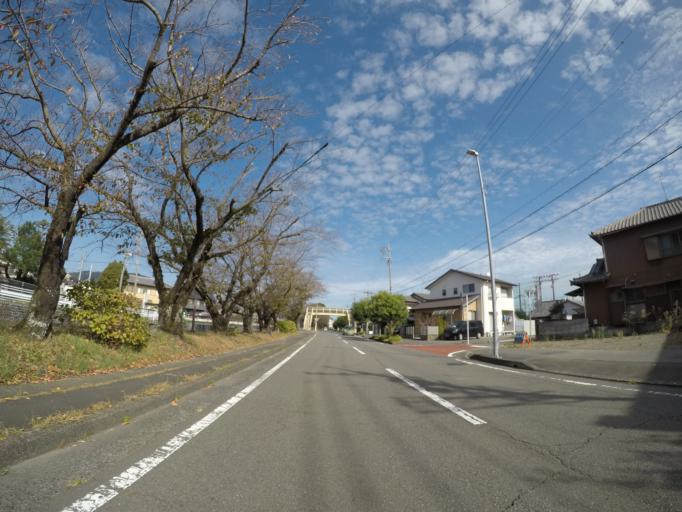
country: JP
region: Shizuoka
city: Yaizu
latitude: 34.8657
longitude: 138.3112
